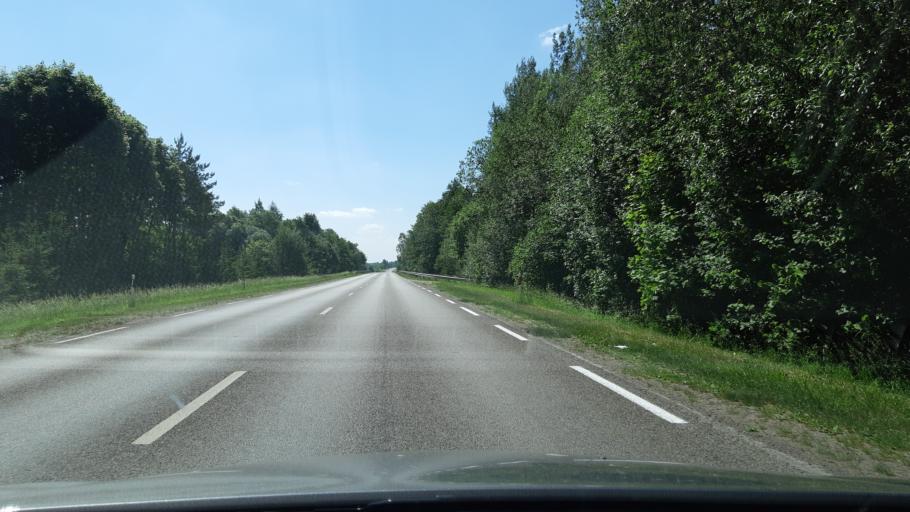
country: LT
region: Alytaus apskritis
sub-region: Alytus
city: Alytus
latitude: 54.4429
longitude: 24.1162
